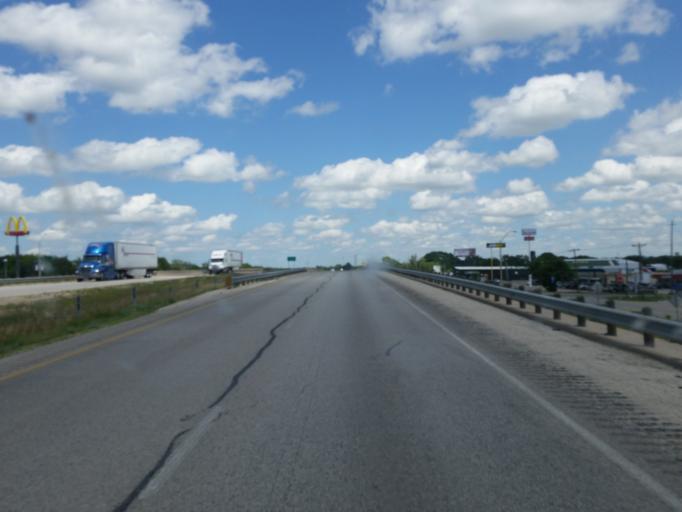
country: US
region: Texas
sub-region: Callahan County
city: Clyde
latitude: 32.4121
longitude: -99.4910
